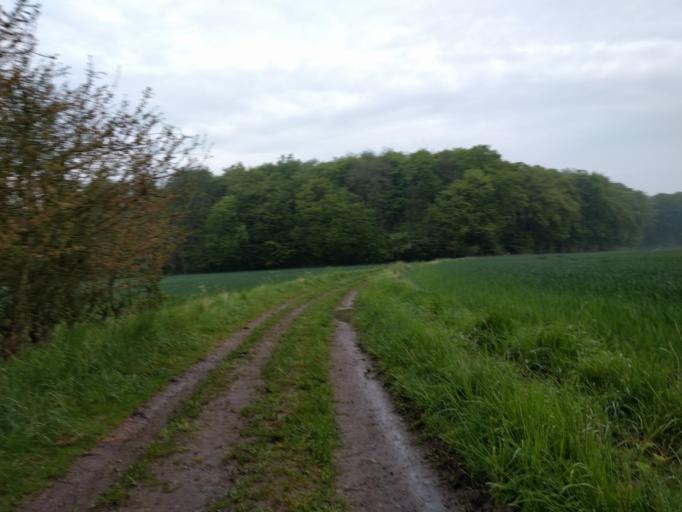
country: DK
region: South Denmark
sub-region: Kerteminde Kommune
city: Munkebo
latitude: 55.4289
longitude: 10.5572
